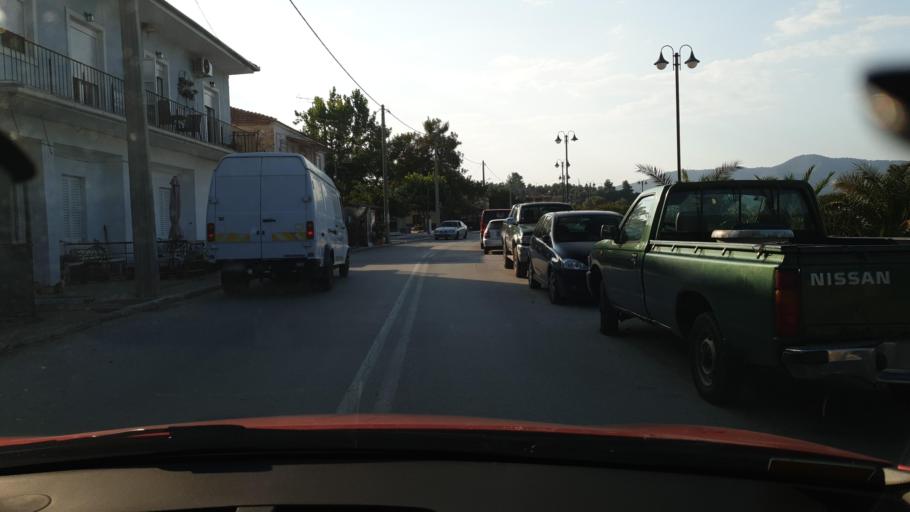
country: GR
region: Thessaly
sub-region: Nomos Magnisias
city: Pteleos
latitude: 39.0057
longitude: 22.9620
